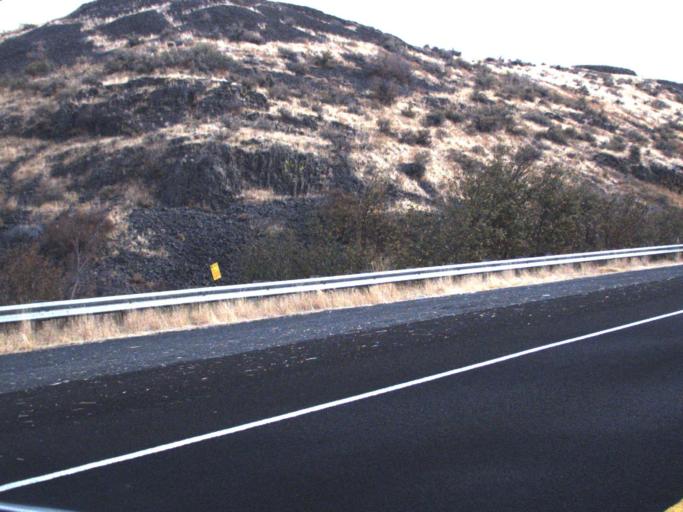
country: US
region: Washington
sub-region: Okanogan County
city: Coulee Dam
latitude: 47.9043
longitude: -118.8695
